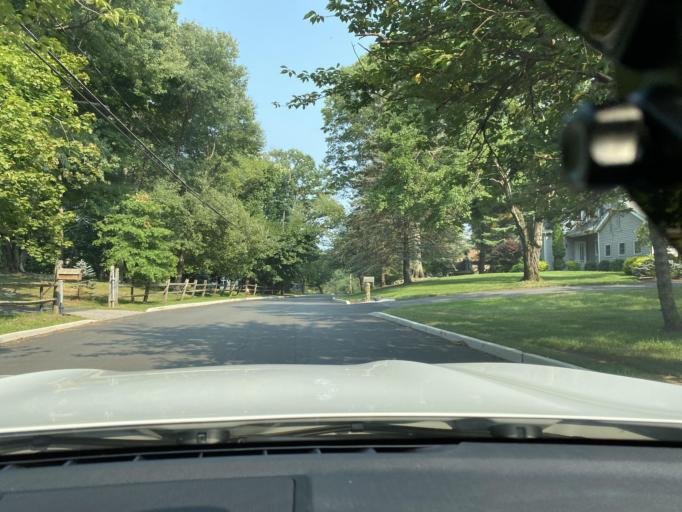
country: US
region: New York
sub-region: Rockland County
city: Airmont
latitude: 41.0871
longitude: -74.1255
